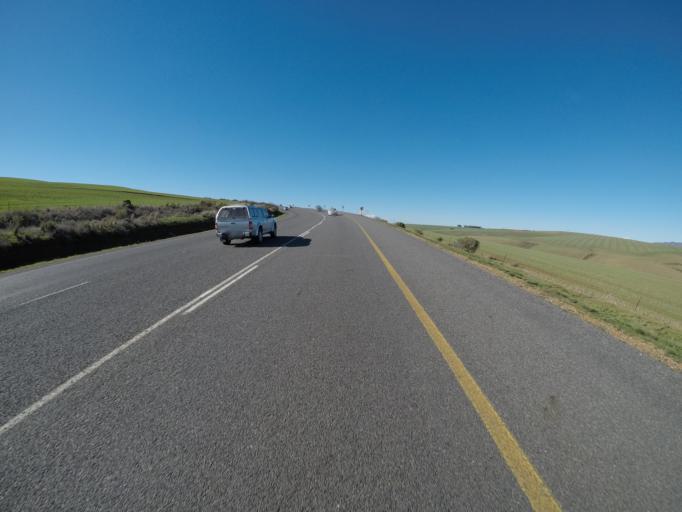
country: ZA
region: Western Cape
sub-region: Overberg District Municipality
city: Caledon
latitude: -34.2294
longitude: 19.2697
